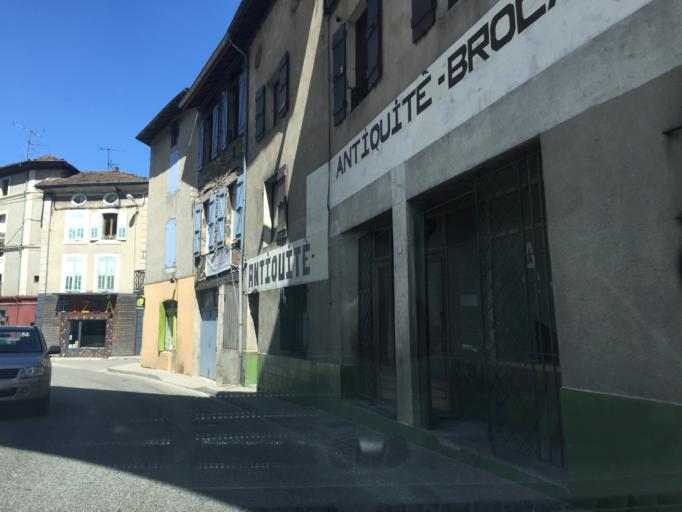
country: FR
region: Rhone-Alpes
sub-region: Departement de l'Isere
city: Saint-Hilaire-du-Rosier
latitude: 45.0599
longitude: 5.2465
